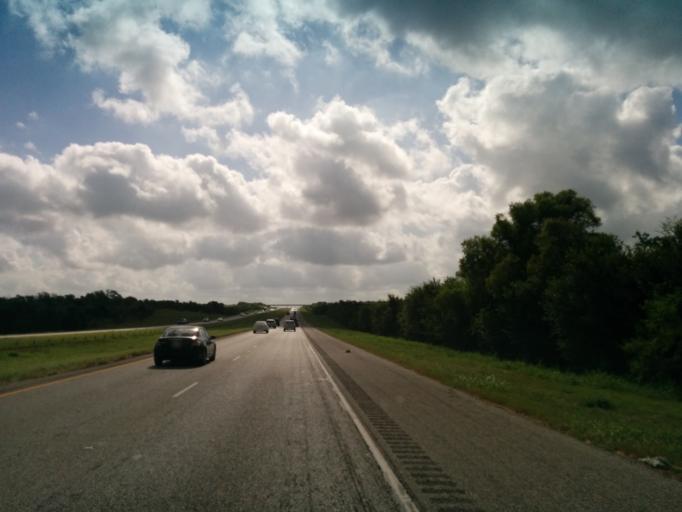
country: US
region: Texas
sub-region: Gonzales County
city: Waelder
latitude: 29.6654
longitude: -97.3468
